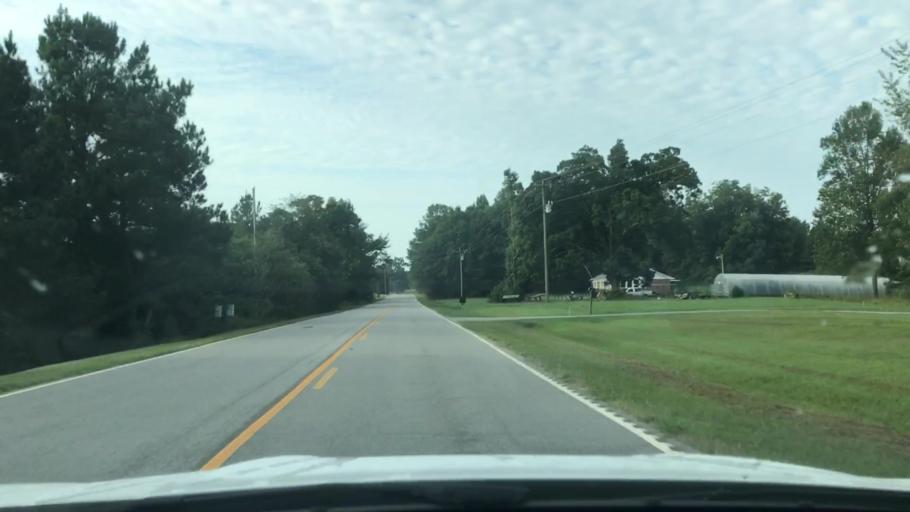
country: US
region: South Carolina
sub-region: Spartanburg County
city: Roebuck
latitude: 34.8263
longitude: -81.9237
